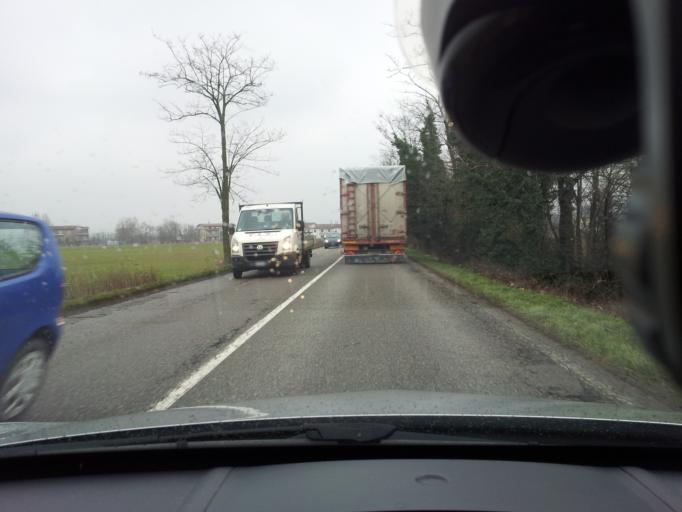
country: IT
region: Lombardy
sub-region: Provincia di Bergamo
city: Calcinate
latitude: 45.6116
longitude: 9.7894
